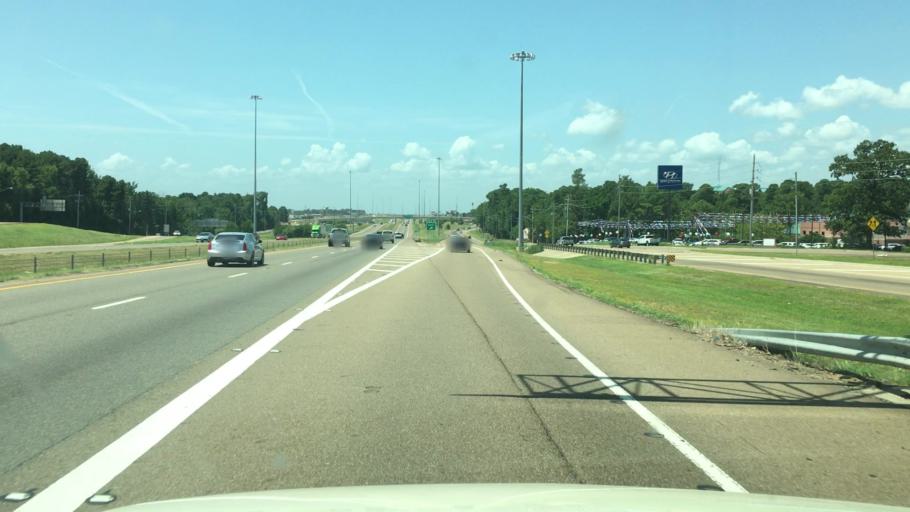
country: US
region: Arkansas
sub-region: Miller County
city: Texarkana
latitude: 33.4650
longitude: -94.0678
